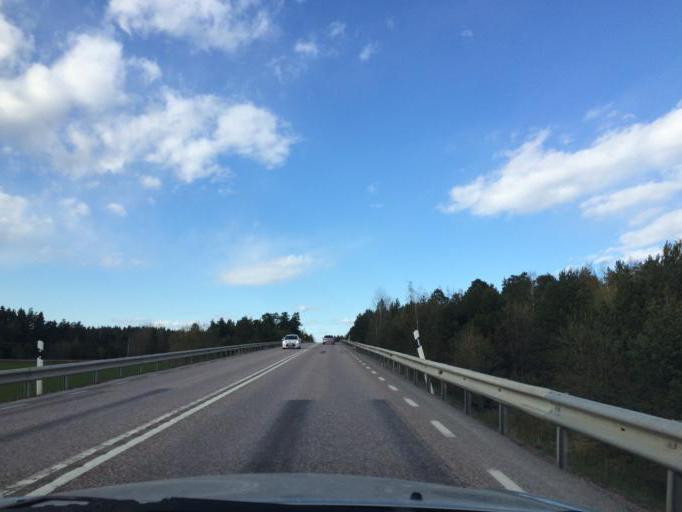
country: SE
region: Vaestmanland
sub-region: Hallstahammars Kommun
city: Kolback
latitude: 59.5625
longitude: 16.3466
